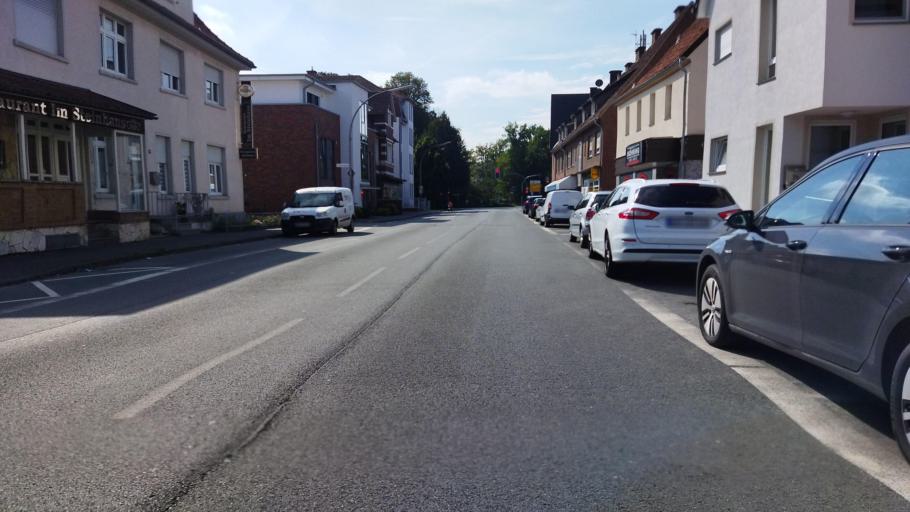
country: DE
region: North Rhine-Westphalia
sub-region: Regierungsbezirk Munster
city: Warendorf
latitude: 51.9564
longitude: 7.9929
